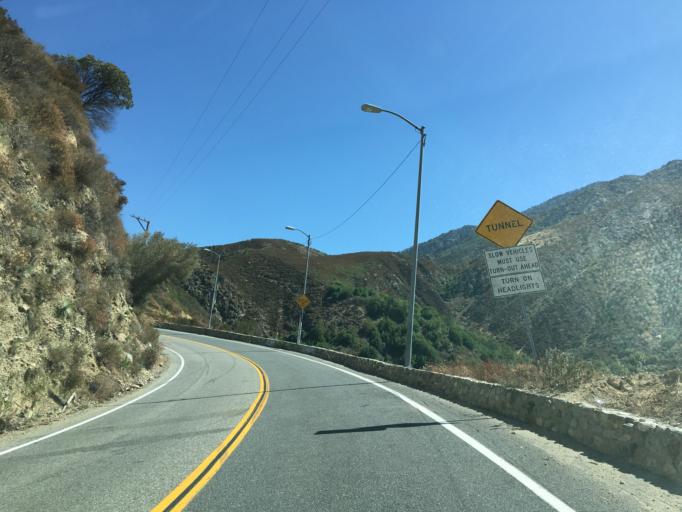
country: US
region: California
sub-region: San Bernardino County
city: San Antonio Heights
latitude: 34.1996
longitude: -117.6761
